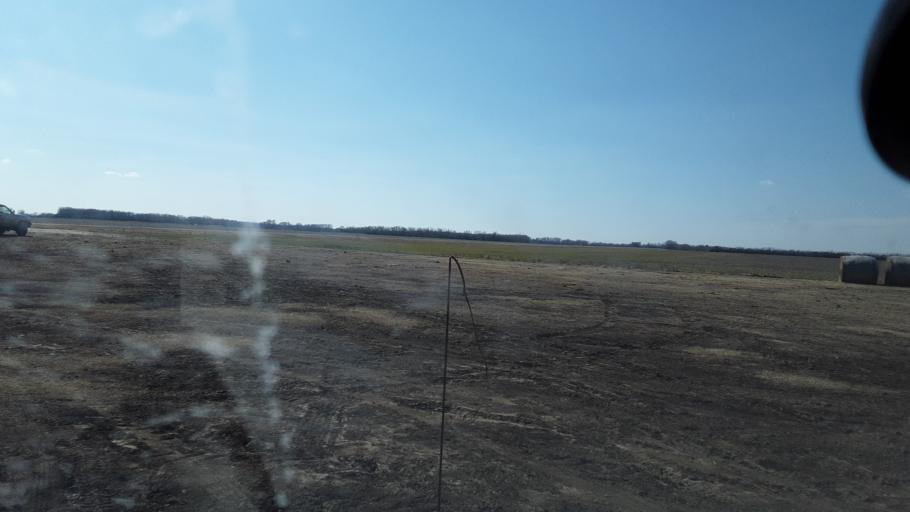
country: US
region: Kansas
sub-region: Reno County
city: South Hutchinson
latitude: 37.9416
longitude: -97.8939
